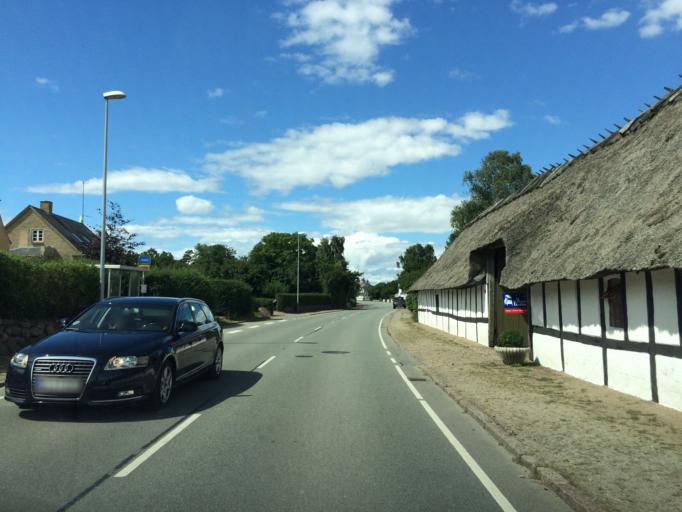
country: DK
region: South Denmark
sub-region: Faaborg-Midtfyn Kommune
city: Faaborg
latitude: 55.1342
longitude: 10.2014
